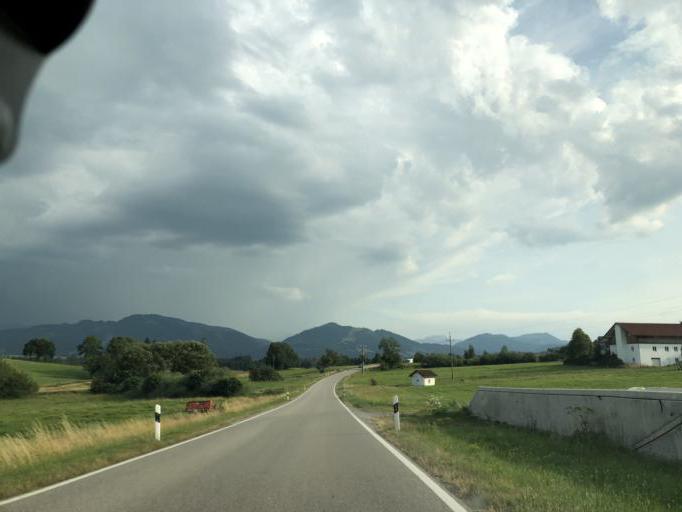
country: DE
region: Bavaria
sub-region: Swabia
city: Gorisried
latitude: 47.6695
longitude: 10.4697
